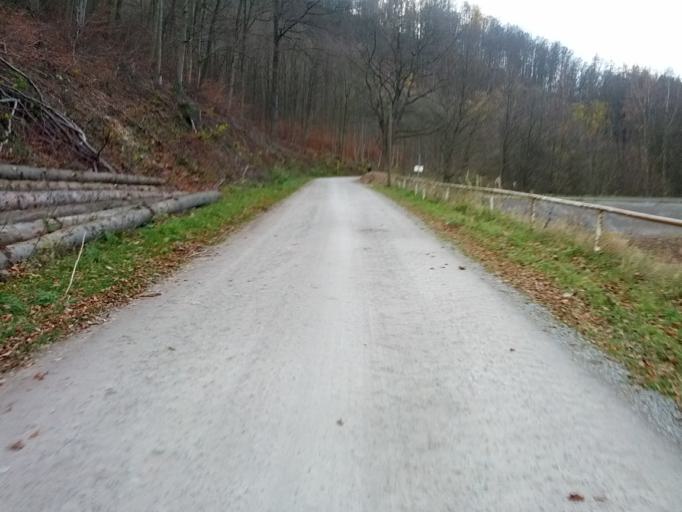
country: DE
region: Thuringia
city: Thal
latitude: 50.9069
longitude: 10.4010
